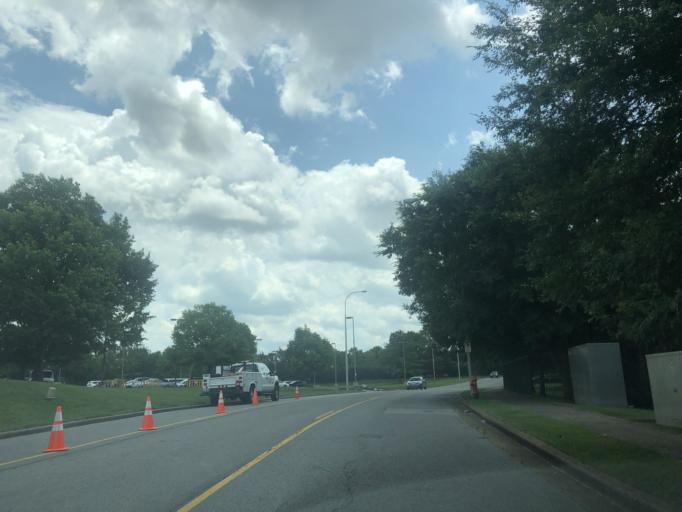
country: US
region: Tennessee
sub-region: Davidson County
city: Nashville
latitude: 36.1891
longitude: -86.8008
